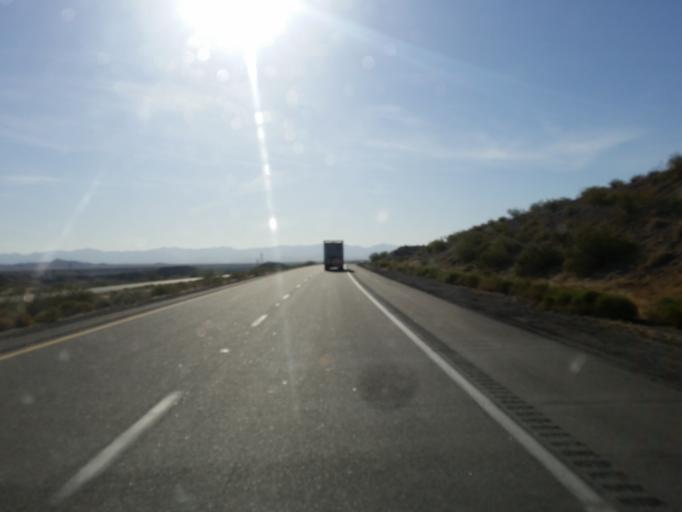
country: US
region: Arizona
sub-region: Mohave County
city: Desert Hills
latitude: 34.7263
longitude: -114.3982
